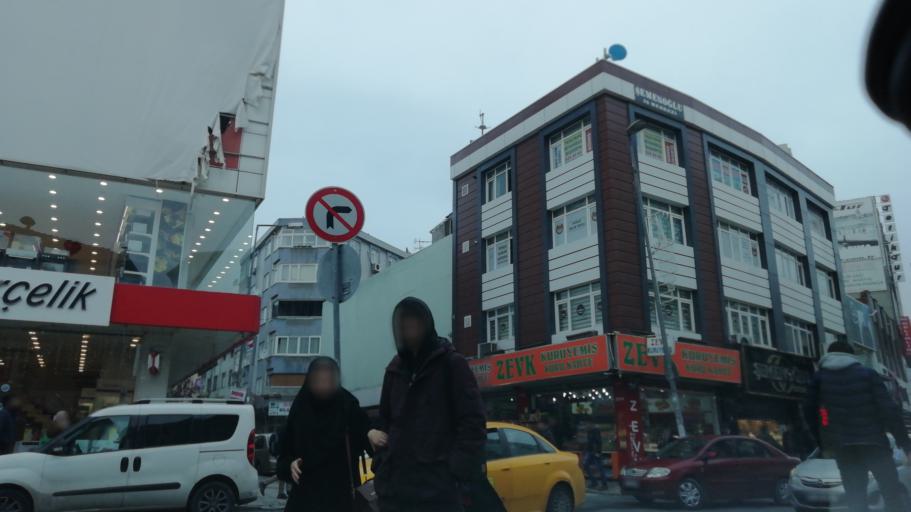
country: TR
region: Istanbul
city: Mahmutbey
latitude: 41.0036
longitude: 28.7983
